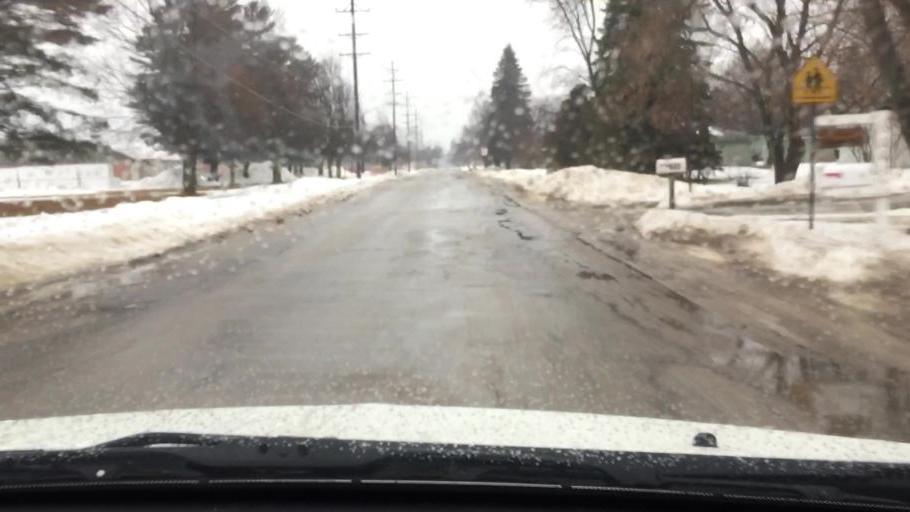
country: US
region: Michigan
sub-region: Charlevoix County
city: Charlevoix
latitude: 45.3081
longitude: -85.2555
